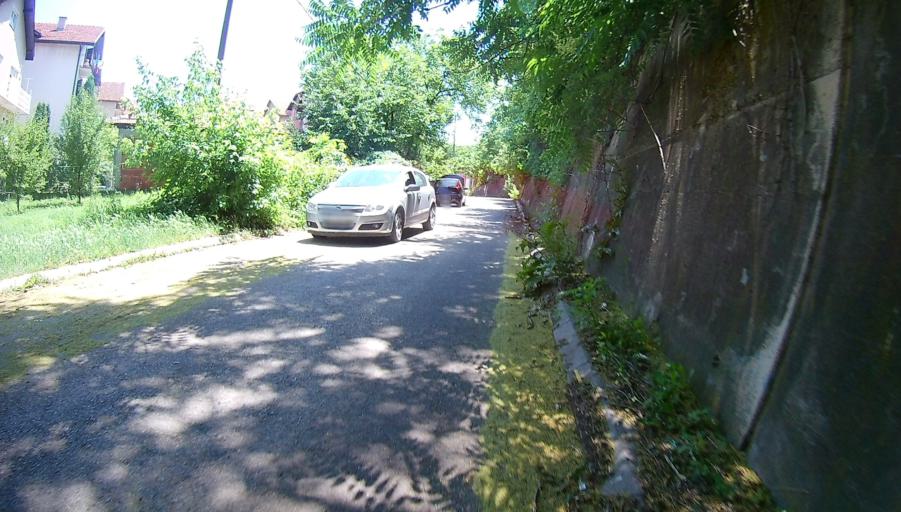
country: RS
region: Central Serbia
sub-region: Nisavski Okrug
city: Nis
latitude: 43.3080
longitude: 21.9170
